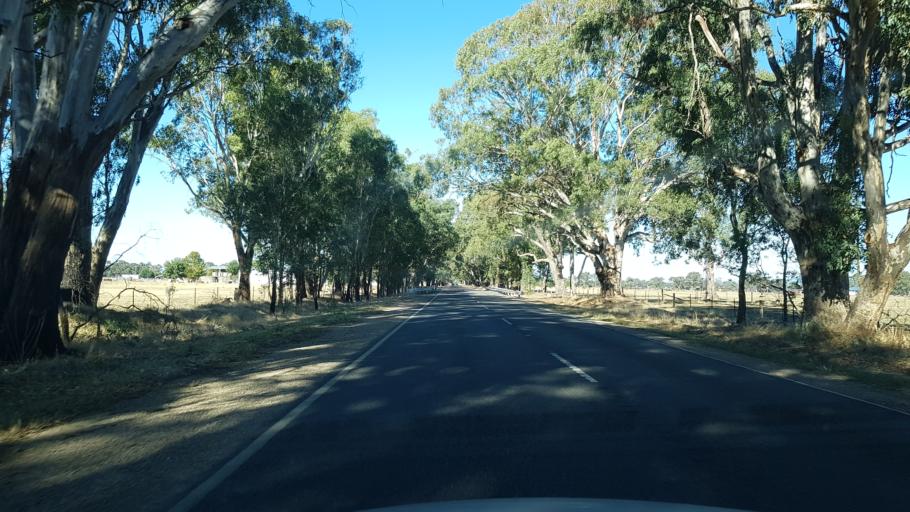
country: AU
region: Victoria
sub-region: Wangaratta
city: Wangaratta
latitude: -36.4345
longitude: 146.3124
